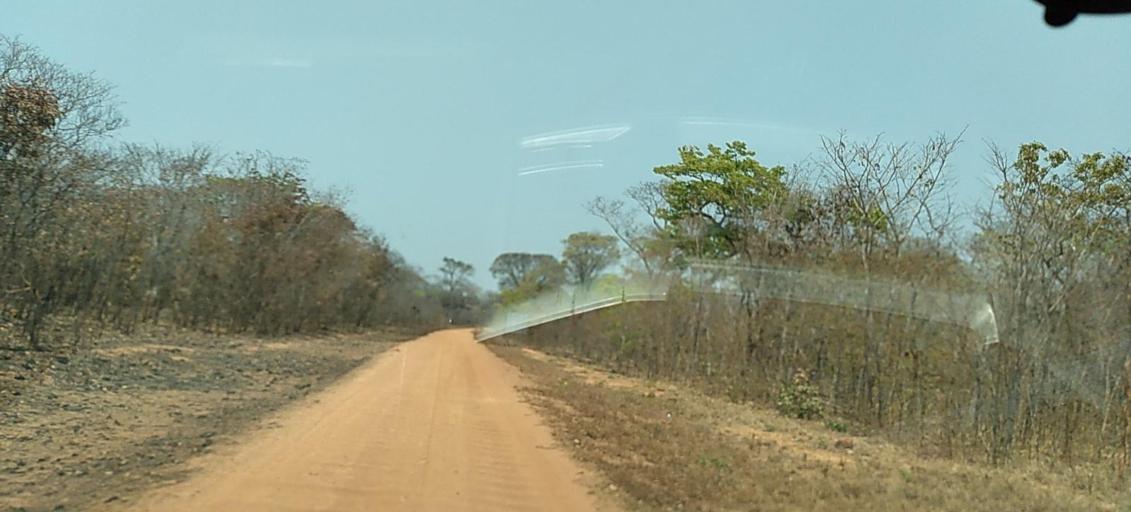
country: ZM
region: Central
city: Mumbwa
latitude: -14.3902
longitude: 26.4887
